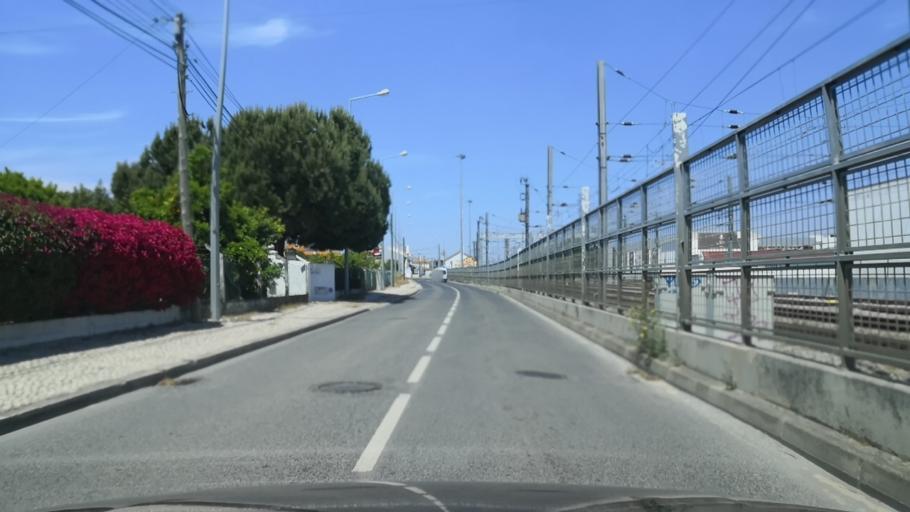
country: PT
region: Setubal
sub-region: Palmela
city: Palmela
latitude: 38.5752
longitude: -8.8736
